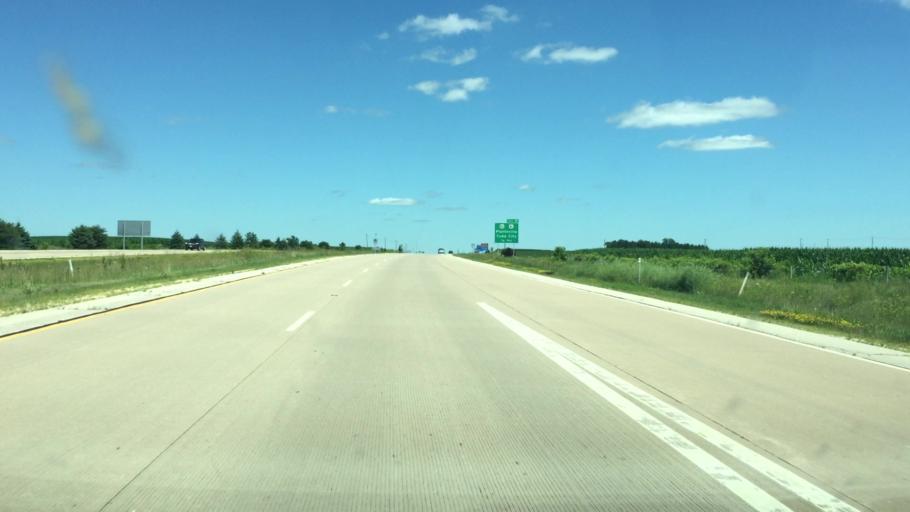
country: US
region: Wisconsin
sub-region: Grant County
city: Platteville
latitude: 42.7134
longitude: -90.4783
